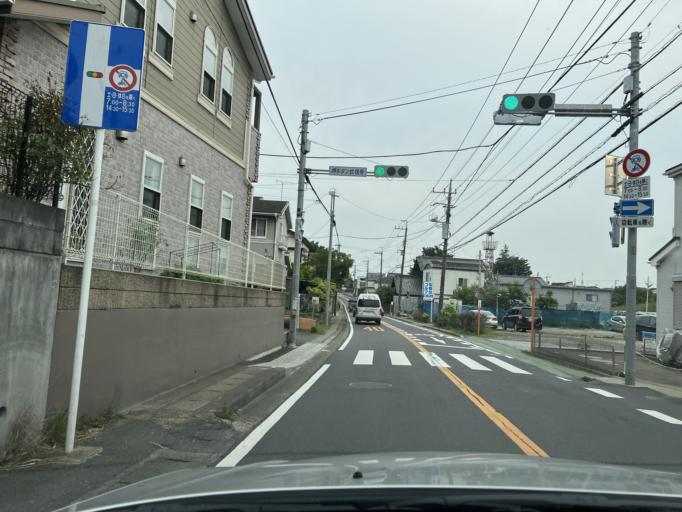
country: JP
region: Chiba
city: Matsudo
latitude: 35.7574
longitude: 139.9398
